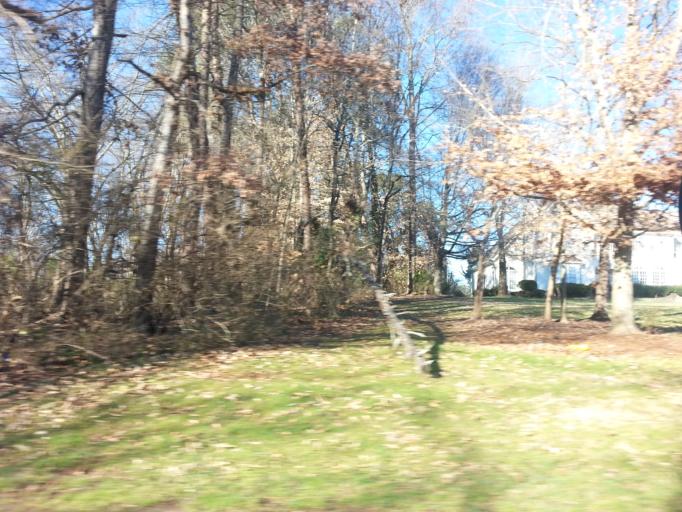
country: US
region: Tennessee
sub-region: Knox County
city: Knoxville
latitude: 35.8902
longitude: -83.9788
